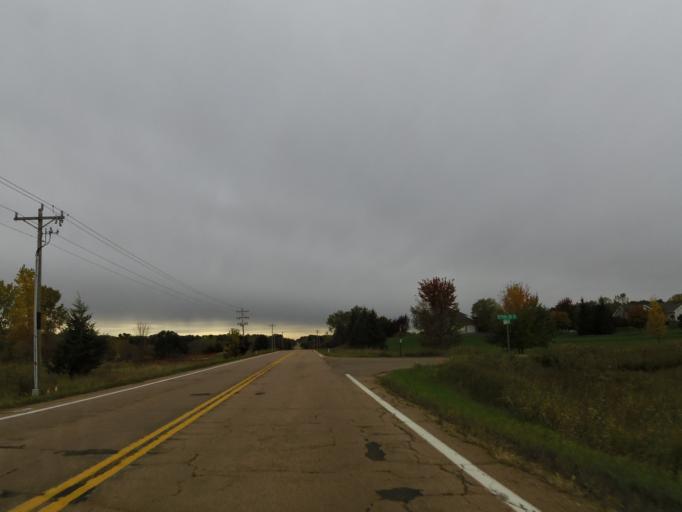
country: US
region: Minnesota
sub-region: Scott County
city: Prior Lake
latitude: 44.6908
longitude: -93.4602
